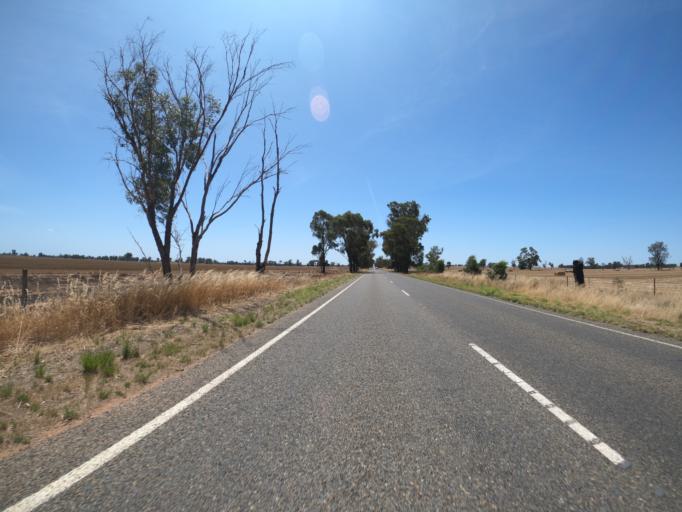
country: AU
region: Victoria
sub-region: Moira
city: Yarrawonga
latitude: -36.0653
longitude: 145.9955
